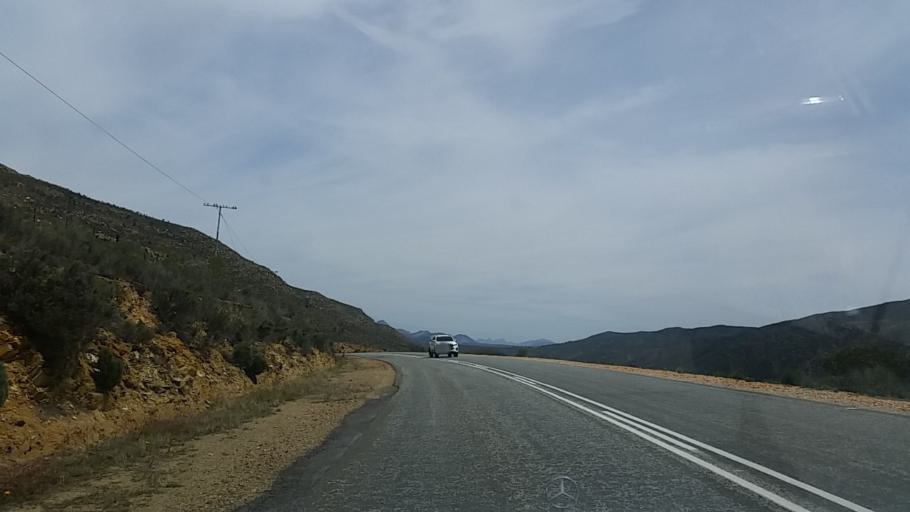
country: ZA
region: Western Cape
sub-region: Eden District Municipality
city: Knysna
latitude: -33.7468
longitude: 22.9822
